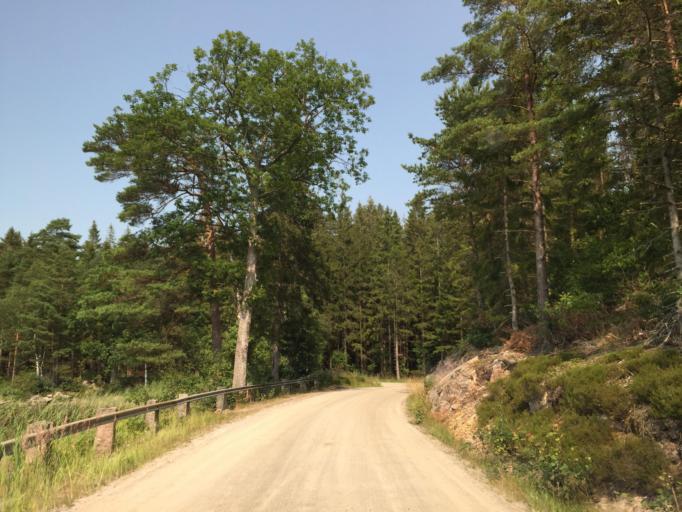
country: SE
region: Vaestra Goetaland
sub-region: Lilla Edets Kommun
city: Lilla Edet
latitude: 58.2304
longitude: 12.1158
